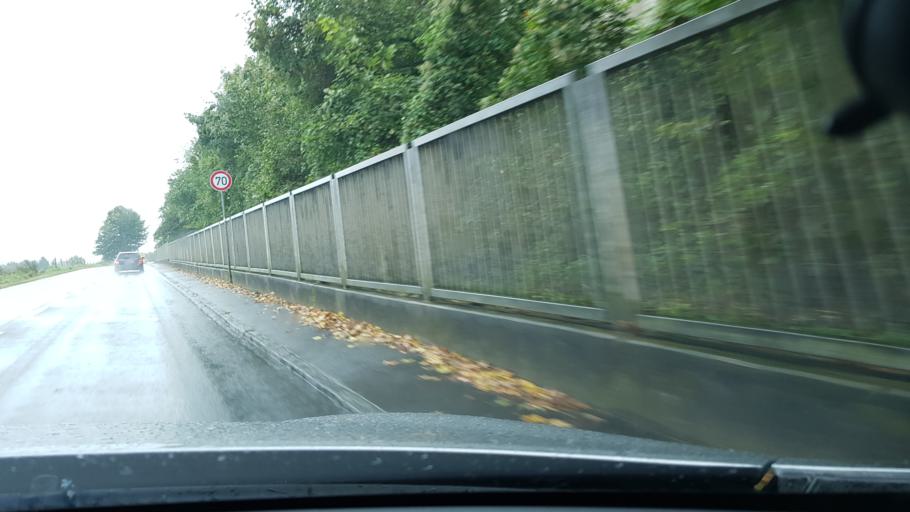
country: DE
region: Rheinland-Pfalz
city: Urbar
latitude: 50.3754
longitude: 7.6322
